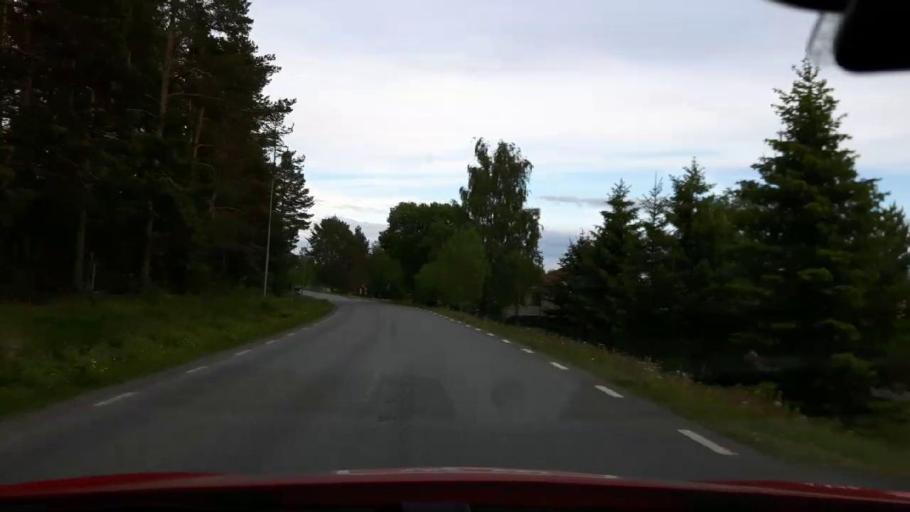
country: SE
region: Jaemtland
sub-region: OEstersunds Kommun
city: Ostersund
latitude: 63.0532
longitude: 14.4502
